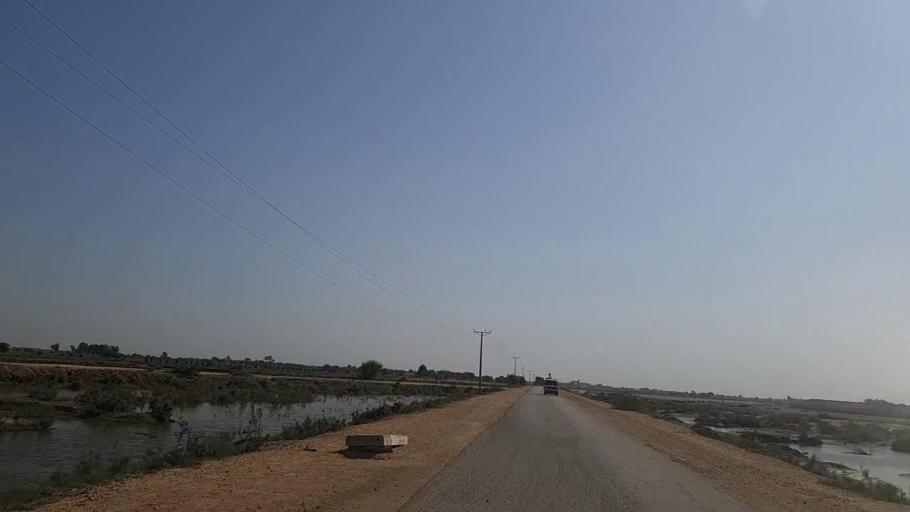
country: PK
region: Sindh
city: Mirpur Batoro
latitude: 24.6312
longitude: 68.2930
